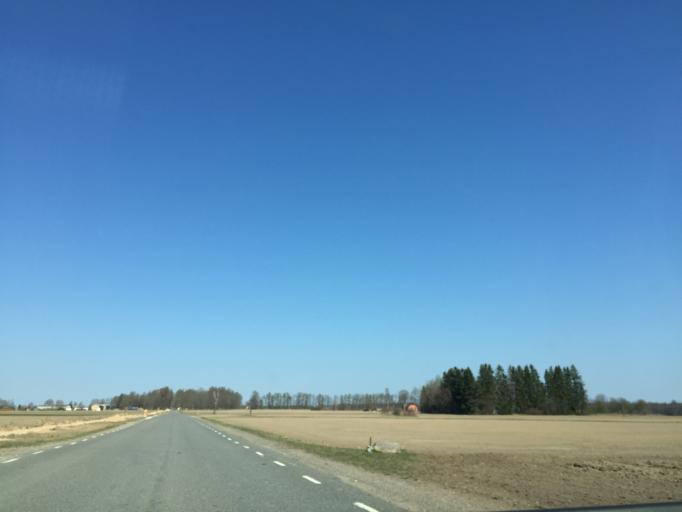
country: EE
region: Tartu
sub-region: Tartu linn
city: Tartu
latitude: 58.5200
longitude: 26.8814
